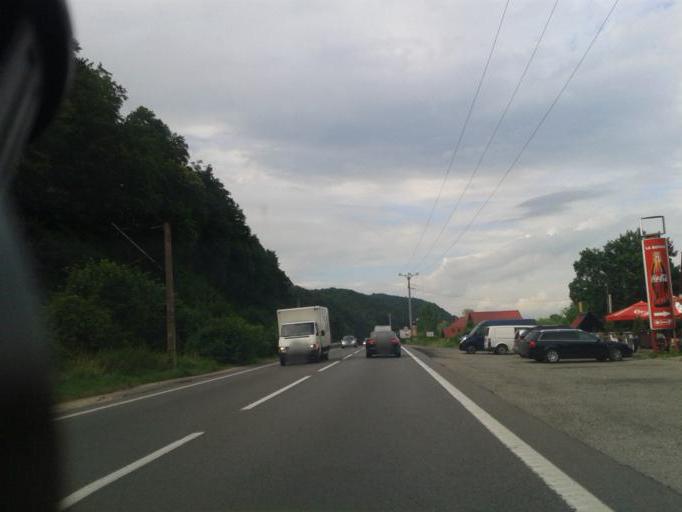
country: RO
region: Brasov
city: Brasov
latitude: 45.5897
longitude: 25.6304
